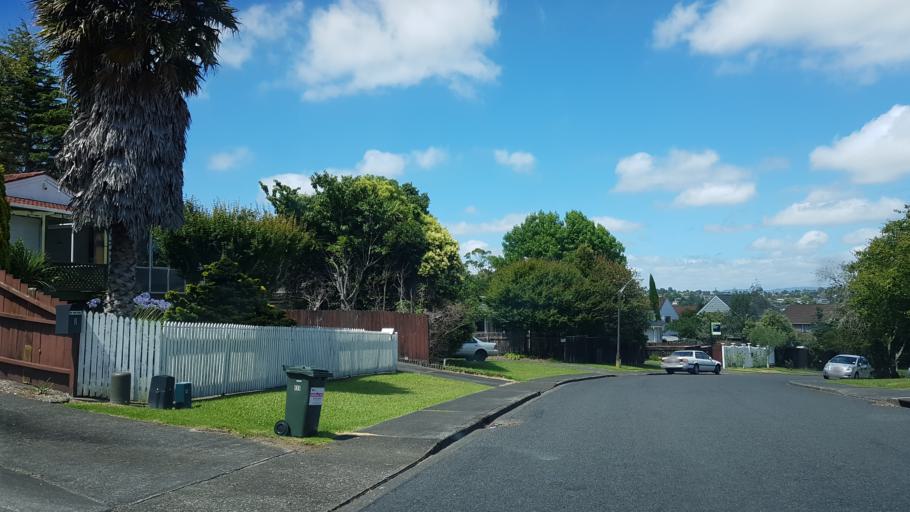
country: NZ
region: Auckland
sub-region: Auckland
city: North Shore
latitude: -36.7887
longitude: 174.7093
